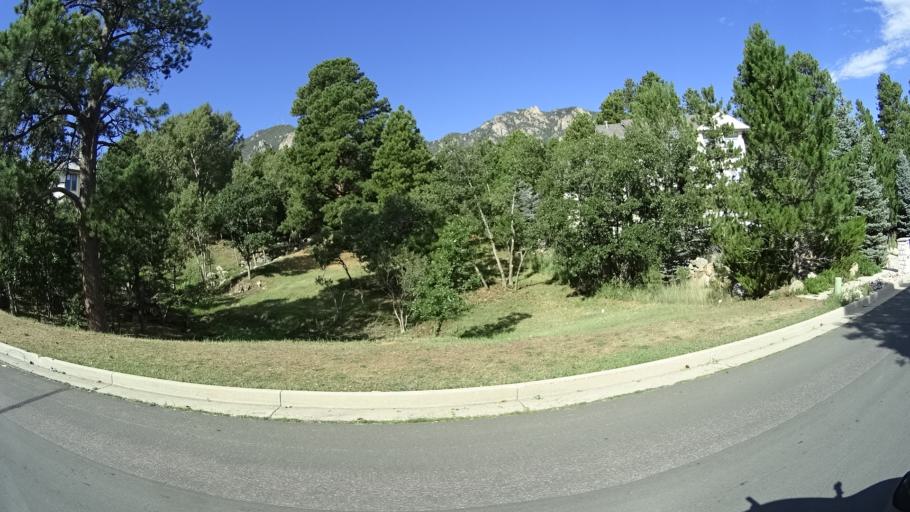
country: US
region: Colorado
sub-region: El Paso County
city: Fort Carson
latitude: 38.7600
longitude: -104.8354
